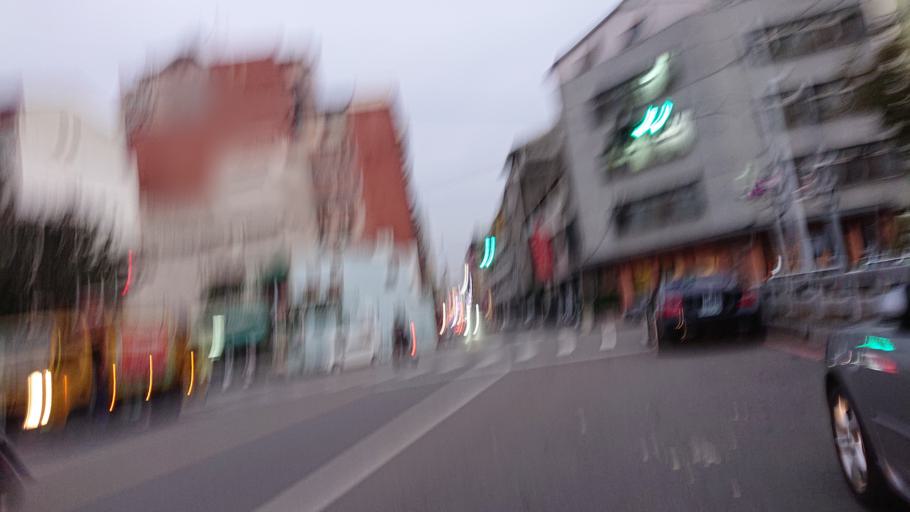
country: TW
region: Taiwan
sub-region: Taichung City
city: Taichung
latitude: 24.1499
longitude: 120.6791
